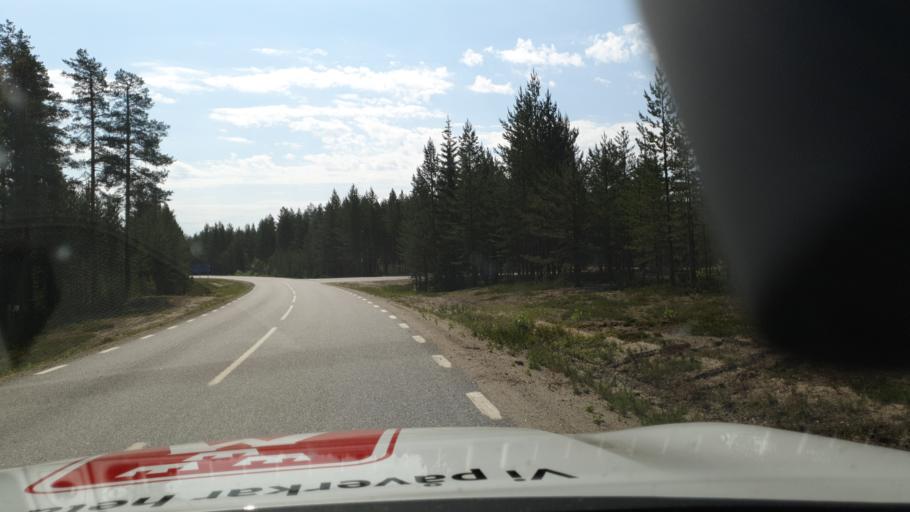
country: SE
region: Vaesterbotten
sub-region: Vindelns Kommun
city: Vindeln
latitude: 64.3865
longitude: 19.3776
